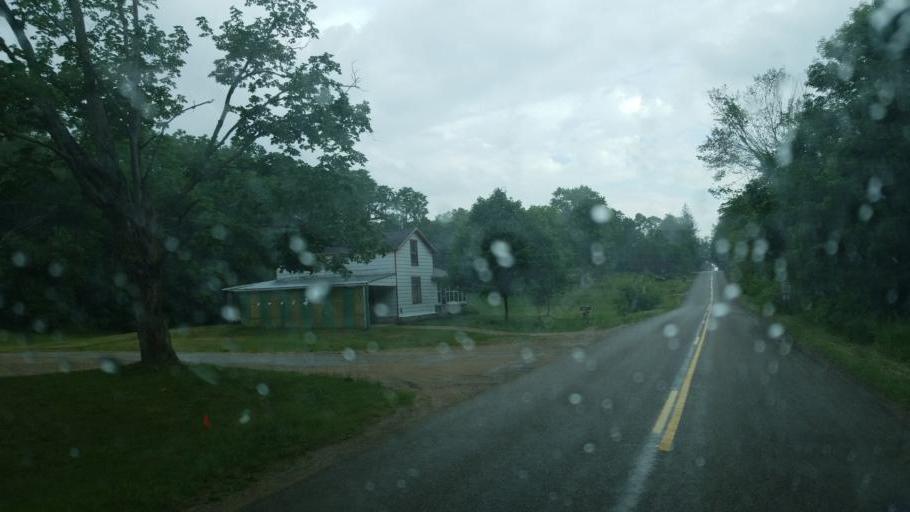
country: US
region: Michigan
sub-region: Barry County
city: Nashville
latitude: 42.5460
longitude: -85.0139
